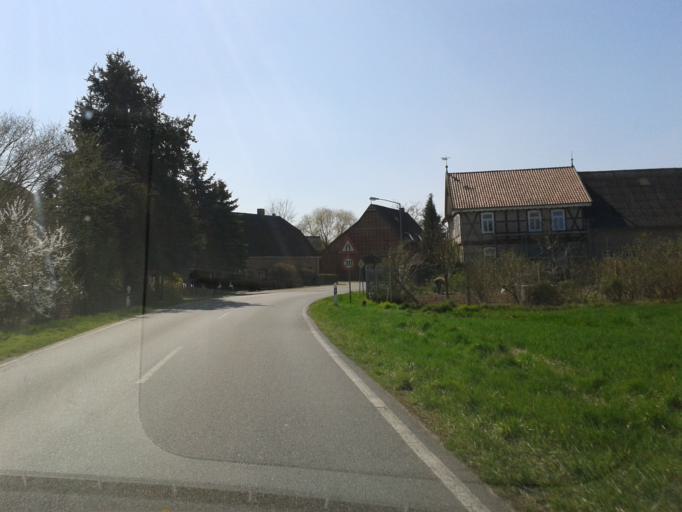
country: DE
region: Lower Saxony
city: Clenze
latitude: 52.9292
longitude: 10.9865
